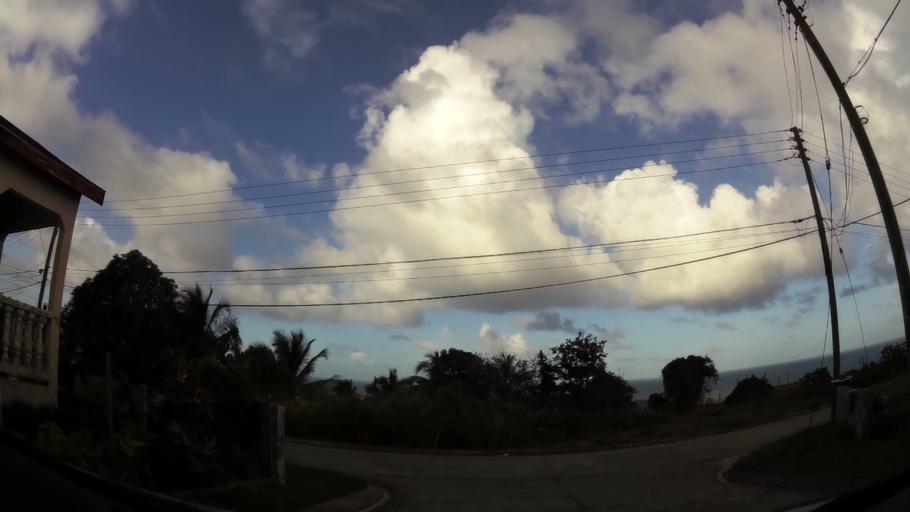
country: KN
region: Saint Mary Cayon
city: Cayon
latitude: 17.3473
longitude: -62.7293
